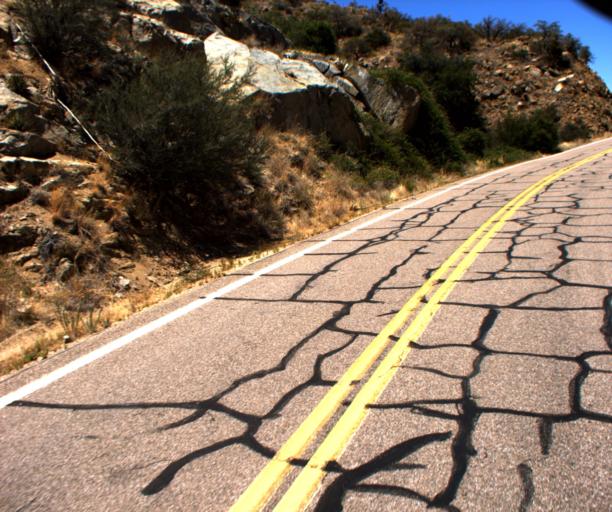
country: US
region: Arizona
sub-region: Pima County
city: Sells
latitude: 31.9690
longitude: -111.6123
